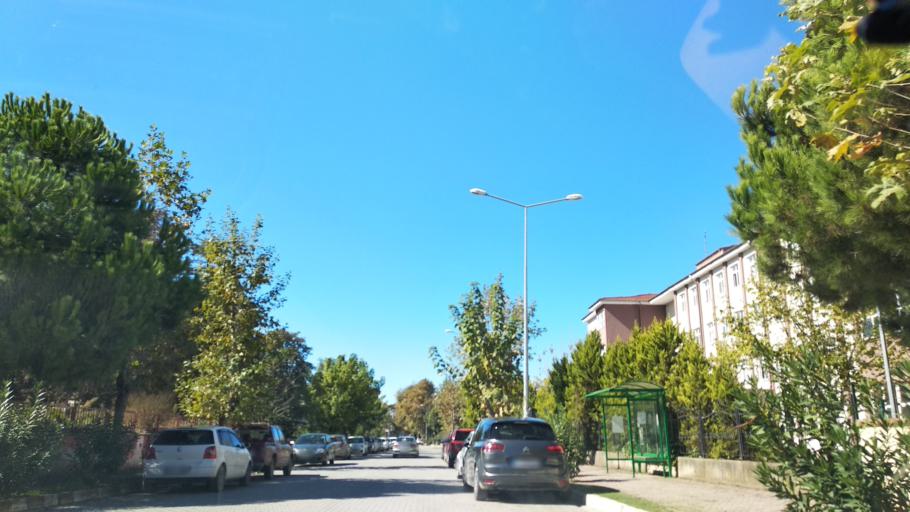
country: TR
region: Sakarya
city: Karasu
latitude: 41.0912
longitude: 30.6997
